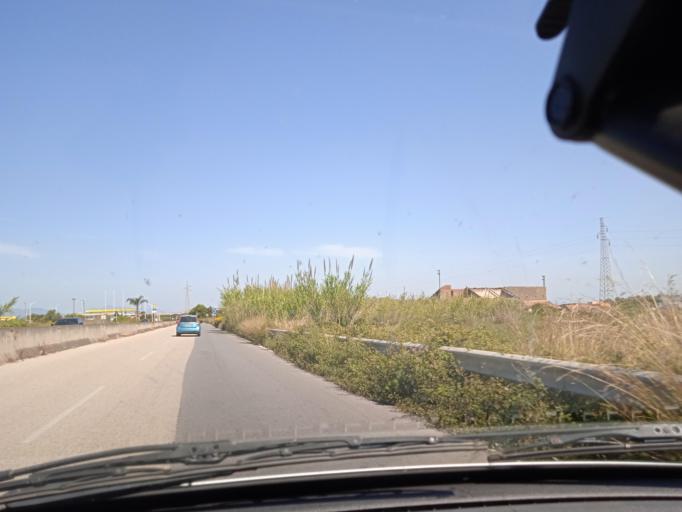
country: IT
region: Sicily
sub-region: Messina
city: San Filippo del Mela
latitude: 38.1908
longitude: 15.2605
